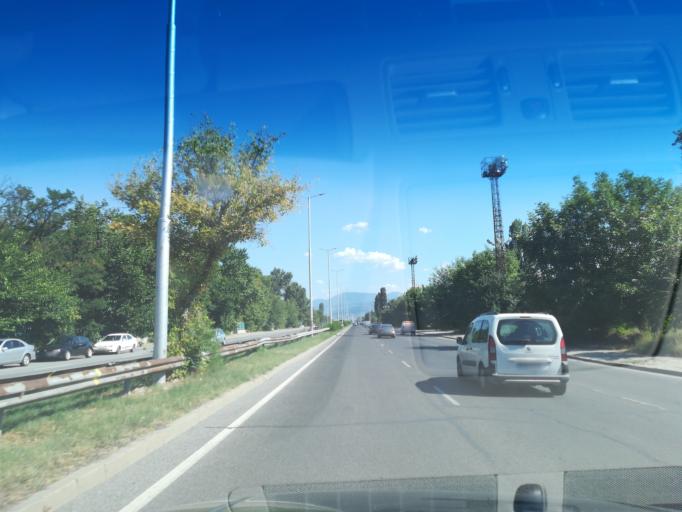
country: BG
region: Plovdiv
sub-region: Obshtina Plovdiv
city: Plovdiv
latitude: 42.1122
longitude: 24.7794
